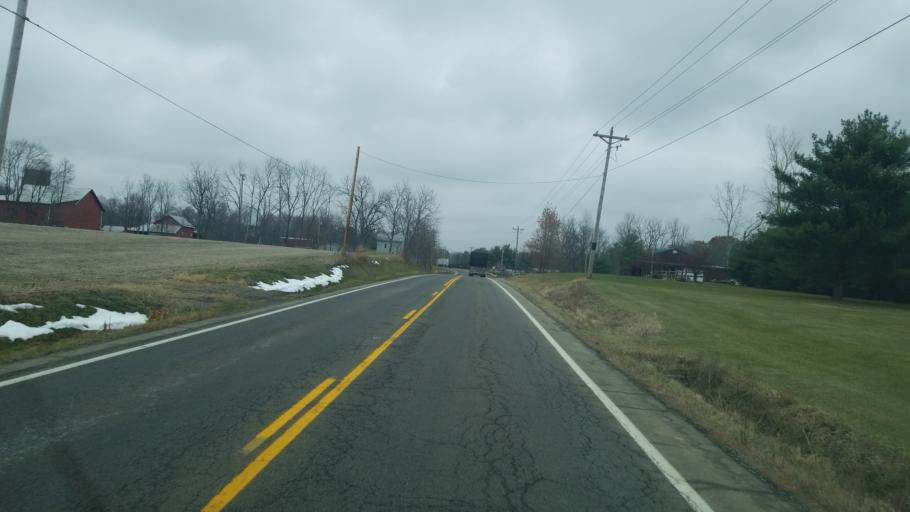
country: US
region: Ohio
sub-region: Huron County
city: Greenwich
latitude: 41.0851
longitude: -82.4874
